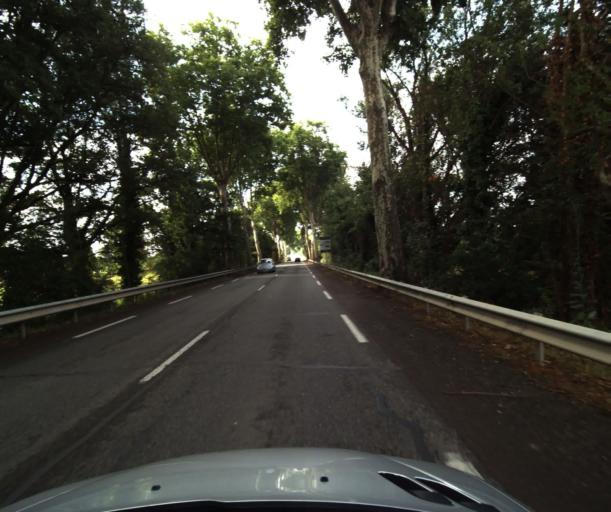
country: FR
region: Midi-Pyrenees
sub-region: Departement du Tarn-et-Garonne
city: Moissac
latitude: 44.0809
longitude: 1.0910
